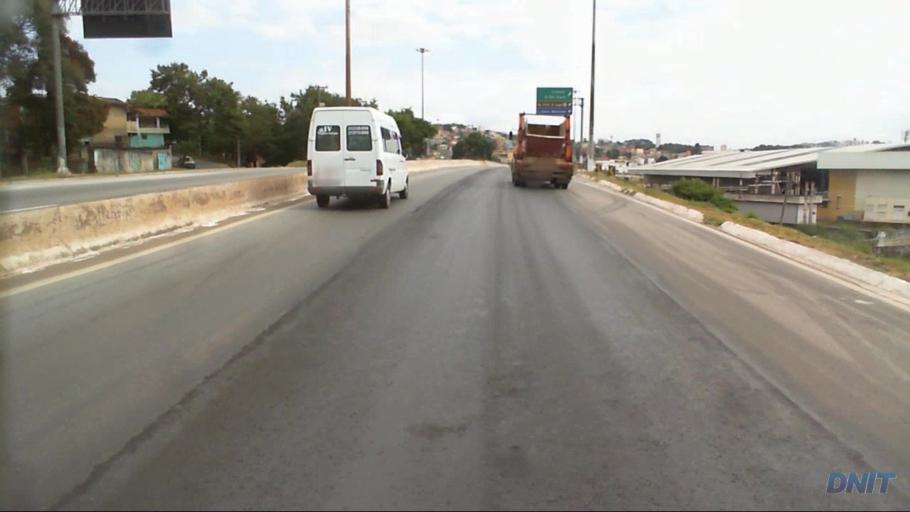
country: BR
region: Minas Gerais
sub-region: Belo Horizonte
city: Belo Horizonte
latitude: -19.8635
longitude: -43.9247
